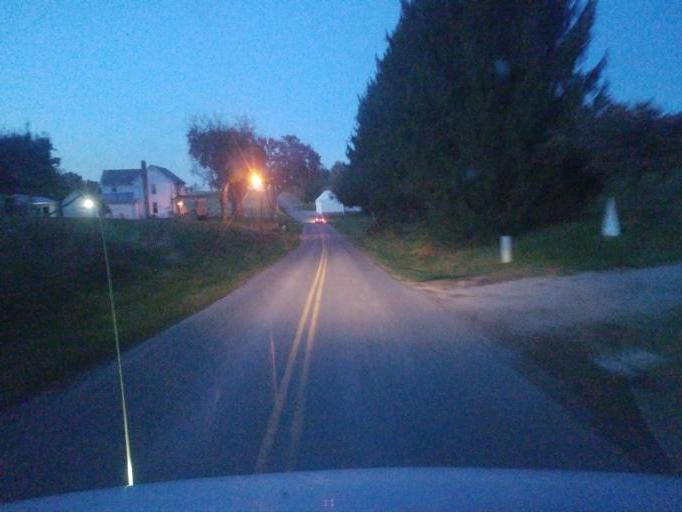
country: US
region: Ohio
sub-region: Perry County
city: Somerset
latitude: 39.8620
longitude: -82.2280
